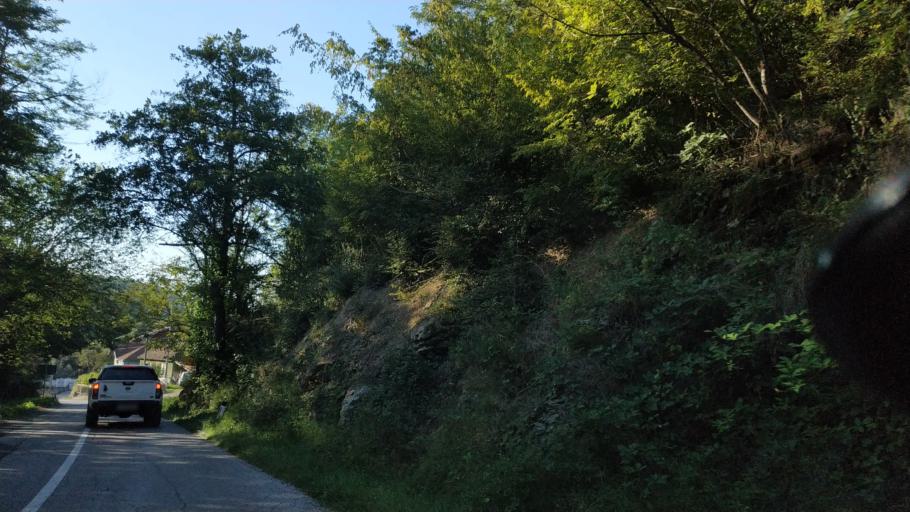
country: RS
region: Central Serbia
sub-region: Rasinski Okrug
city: Krusevac
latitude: 43.4702
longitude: 21.3572
